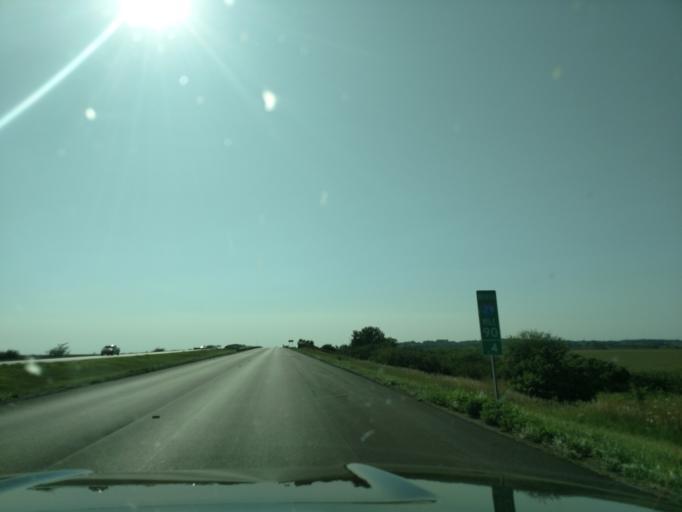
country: US
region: Missouri
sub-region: Holt County
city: Mound City
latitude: 40.1840
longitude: -95.3277
